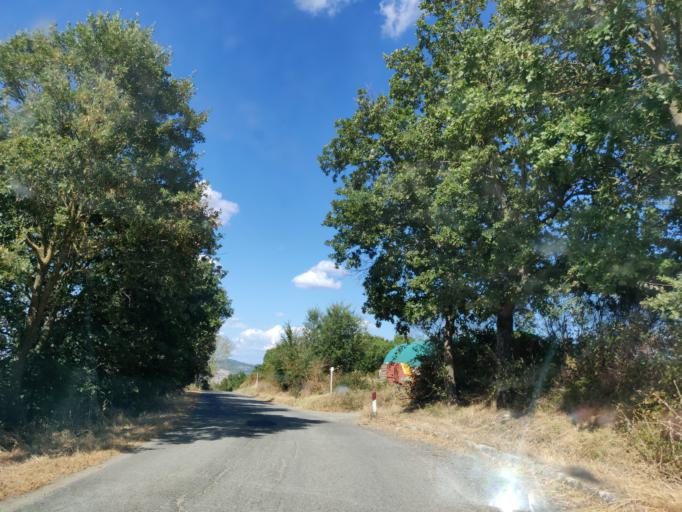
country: IT
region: Tuscany
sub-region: Provincia di Siena
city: Radicofani
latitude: 42.9622
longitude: 11.7276
